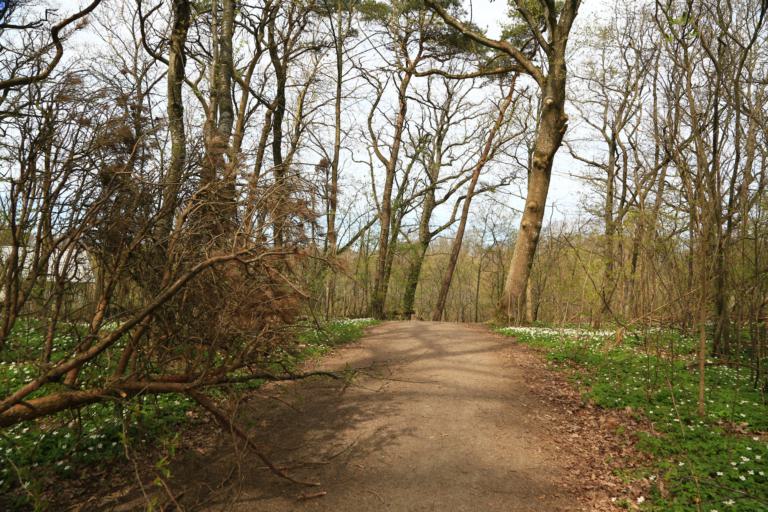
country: SE
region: Halland
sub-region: Varbergs Kommun
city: Varberg
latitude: 57.1318
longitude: 12.2781
